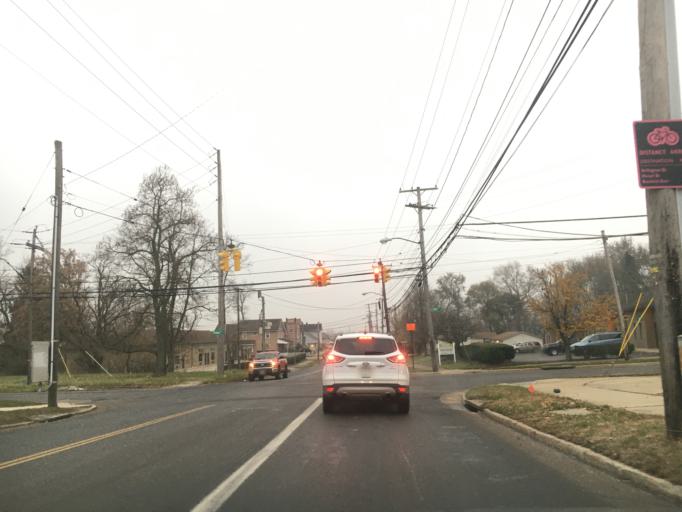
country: US
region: Ohio
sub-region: Summit County
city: Akron
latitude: 41.0949
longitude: -81.4880
